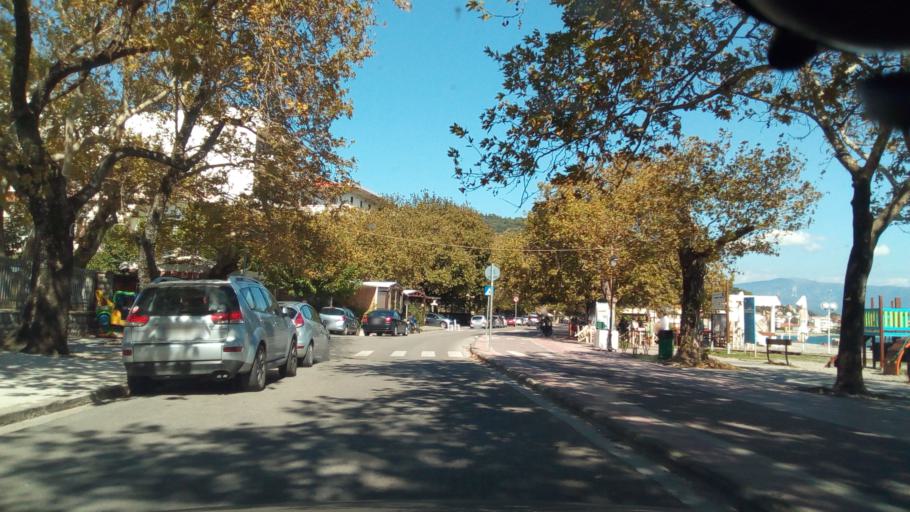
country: GR
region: West Greece
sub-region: Nomos Aitolias kai Akarnanias
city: Nafpaktos
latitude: 38.3902
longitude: 21.8238
